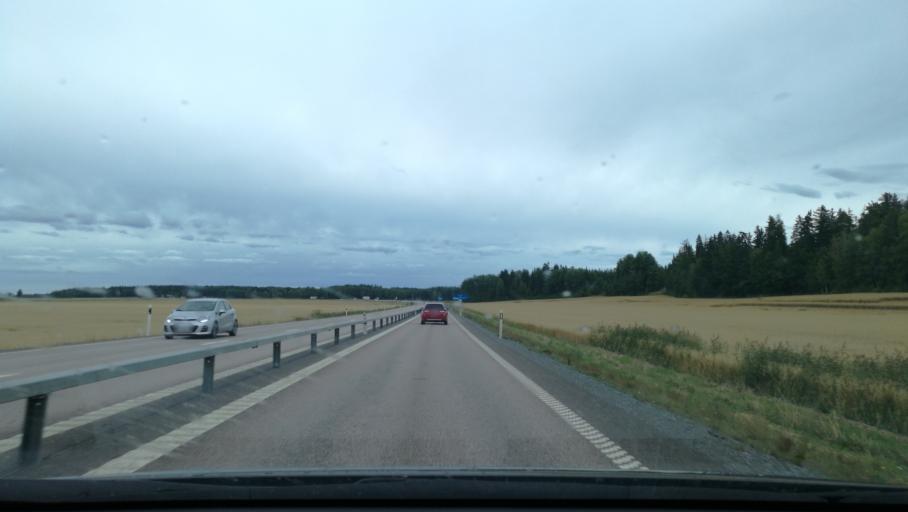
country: SE
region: Vaestmanland
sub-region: Vasteras
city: Hokasen
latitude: 59.7030
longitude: 16.5786
